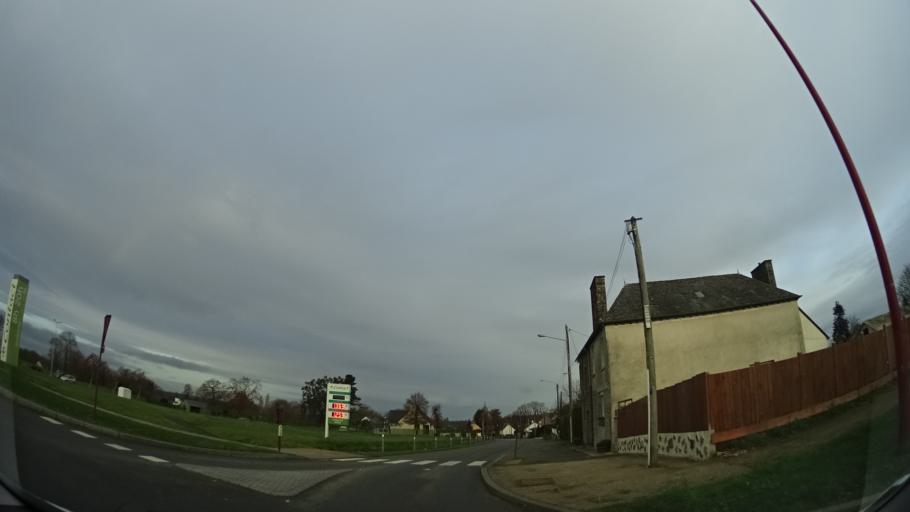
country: FR
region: Brittany
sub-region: Departement des Cotes-d'Armor
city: Evran
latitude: 48.3759
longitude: -1.9742
